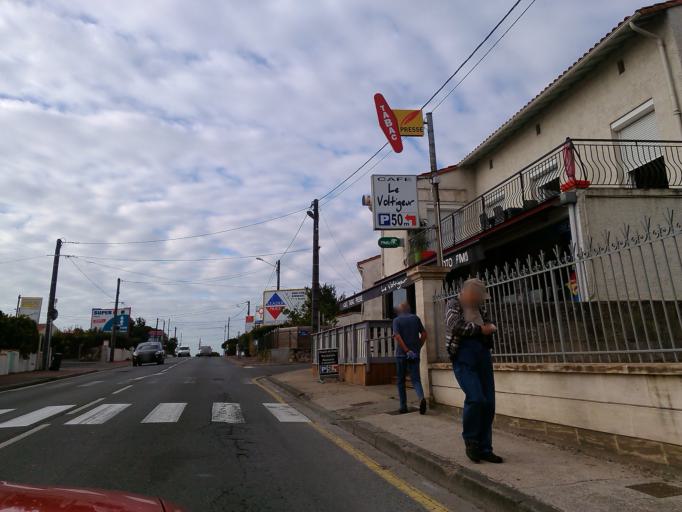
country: FR
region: Poitou-Charentes
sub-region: Departement de la Charente-Maritime
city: Royan
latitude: 45.6433
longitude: -1.0249
